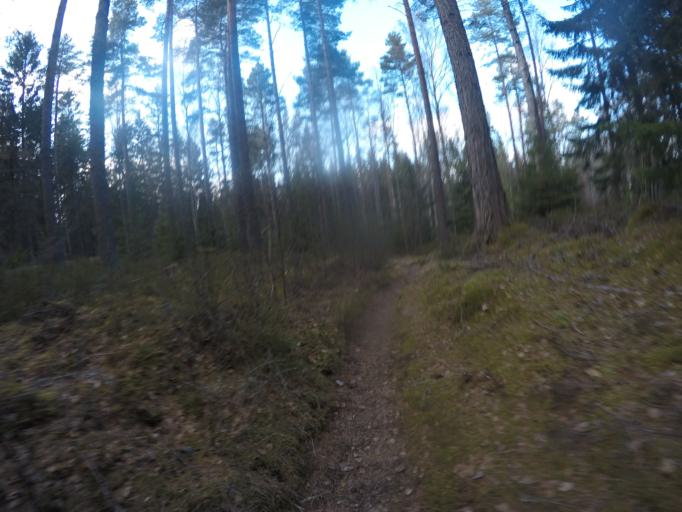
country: SE
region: Soedermanland
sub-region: Eskilstuna Kommun
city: Hallbybrunn
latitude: 59.3896
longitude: 16.4027
